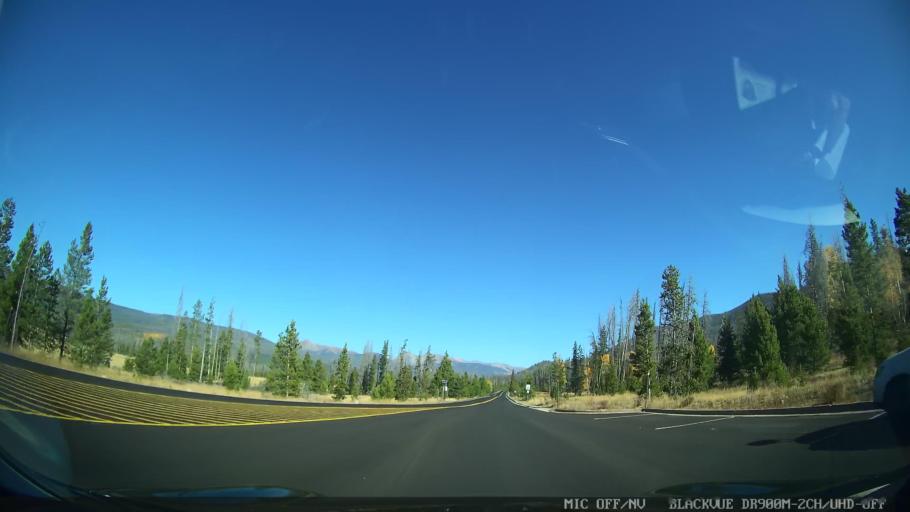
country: US
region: Colorado
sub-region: Grand County
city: Granby
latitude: 40.2723
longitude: -105.8349
